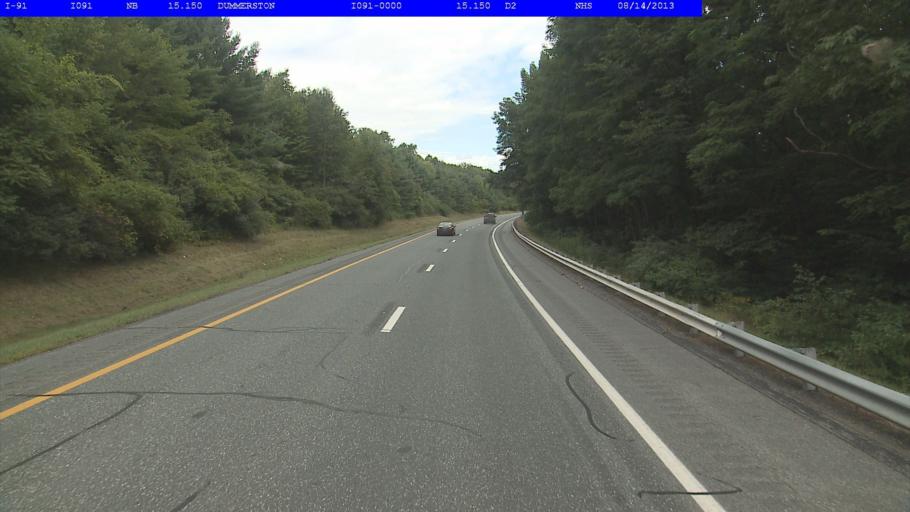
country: US
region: New Hampshire
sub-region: Cheshire County
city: Chesterfield
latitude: 42.9283
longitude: -72.5281
